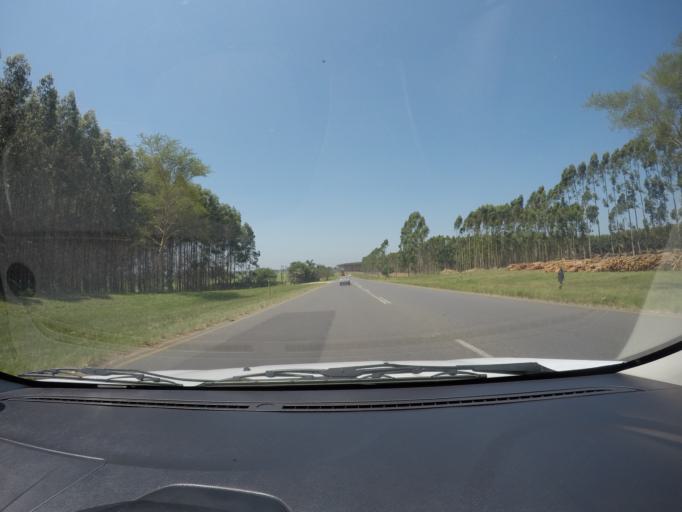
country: ZA
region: KwaZulu-Natal
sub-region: uThungulu District Municipality
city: eSikhawini
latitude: -28.8191
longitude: 31.9511
